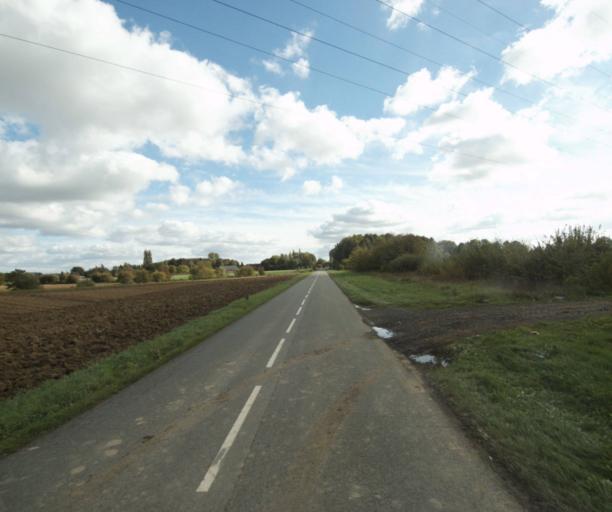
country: FR
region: Nord-Pas-de-Calais
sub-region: Departement du Nord
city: Bois-Grenier
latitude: 50.6598
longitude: 2.9025
